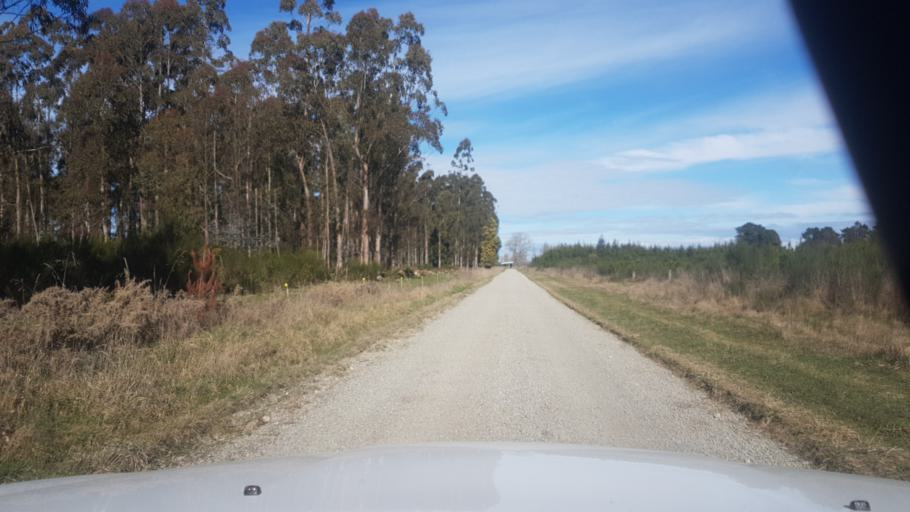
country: NZ
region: Canterbury
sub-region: Timaru District
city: Pleasant Point
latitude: -44.1405
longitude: 171.2755
